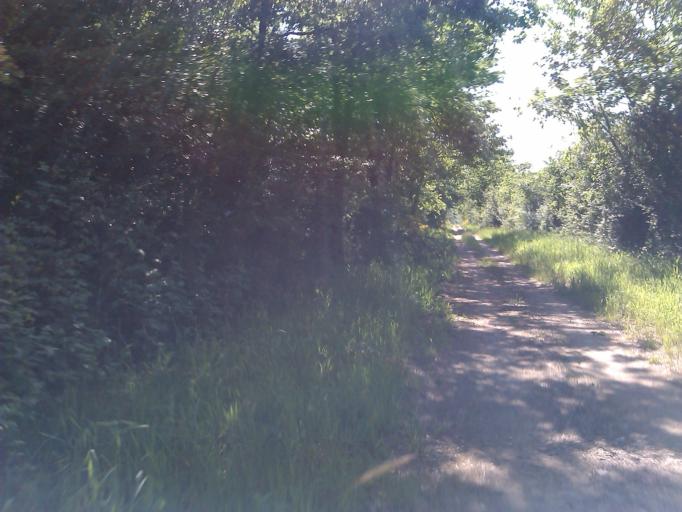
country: FR
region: Centre
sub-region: Departement de l'Indre
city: Belabre
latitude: 46.6270
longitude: 1.2227
